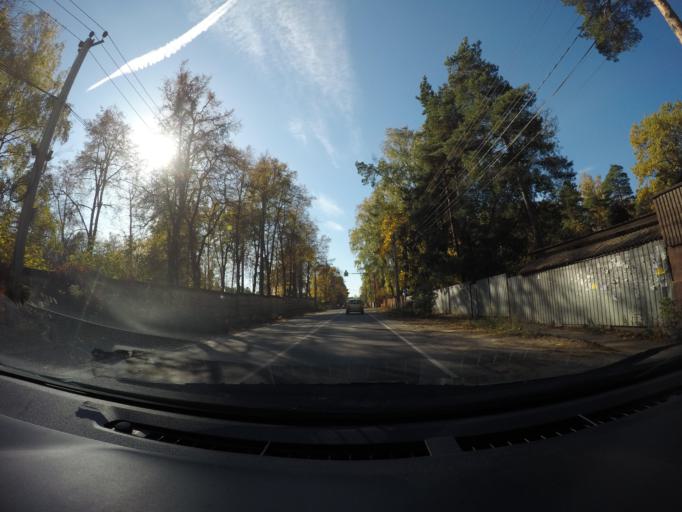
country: RU
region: Moskovskaya
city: Rodniki
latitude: 55.6366
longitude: 38.0525
